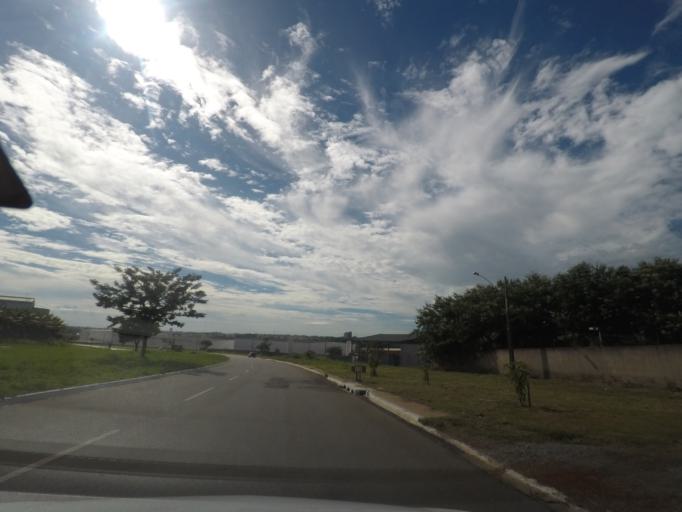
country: BR
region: Goias
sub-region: Aparecida De Goiania
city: Aparecida de Goiania
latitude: -16.8088
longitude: -49.2693
